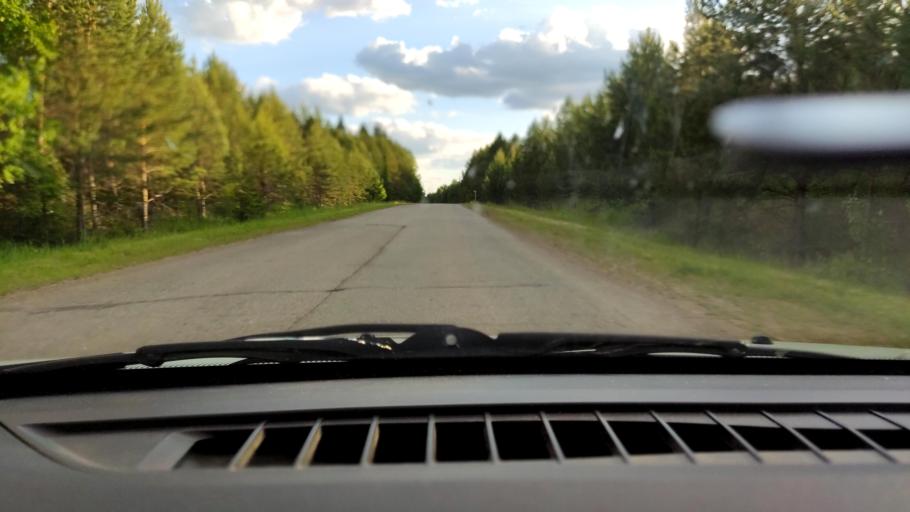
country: RU
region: Perm
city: Uinskoye
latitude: 57.0873
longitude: 56.6259
